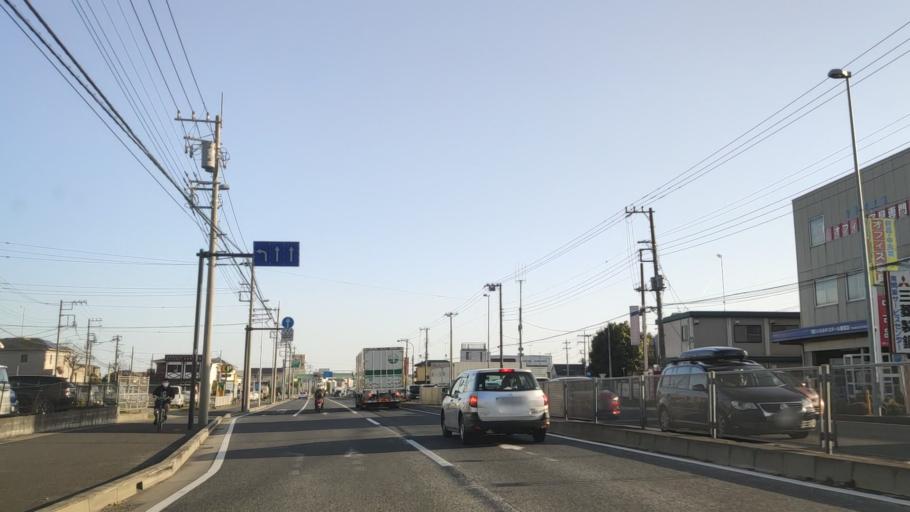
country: JP
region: Kanagawa
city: Zama
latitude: 35.4774
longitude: 139.3665
